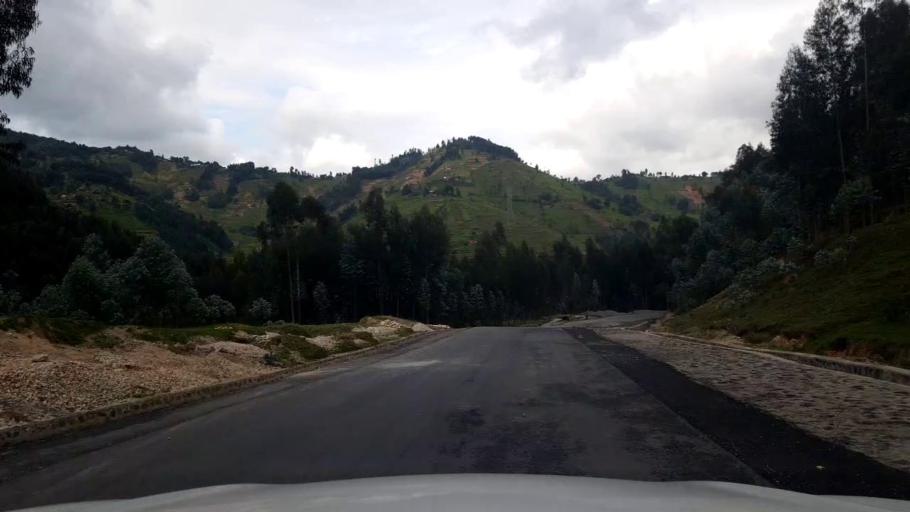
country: RW
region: Northern Province
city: Musanze
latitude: -1.6853
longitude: 29.5251
